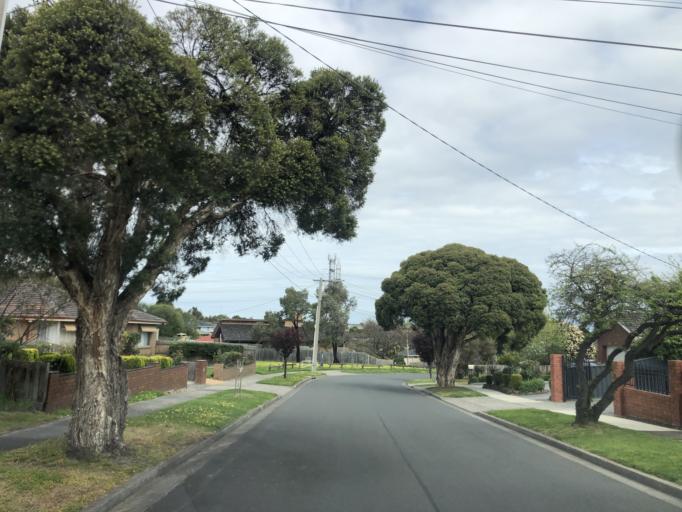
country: AU
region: Victoria
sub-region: Monash
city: Chadstone
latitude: -37.8834
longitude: 145.1047
